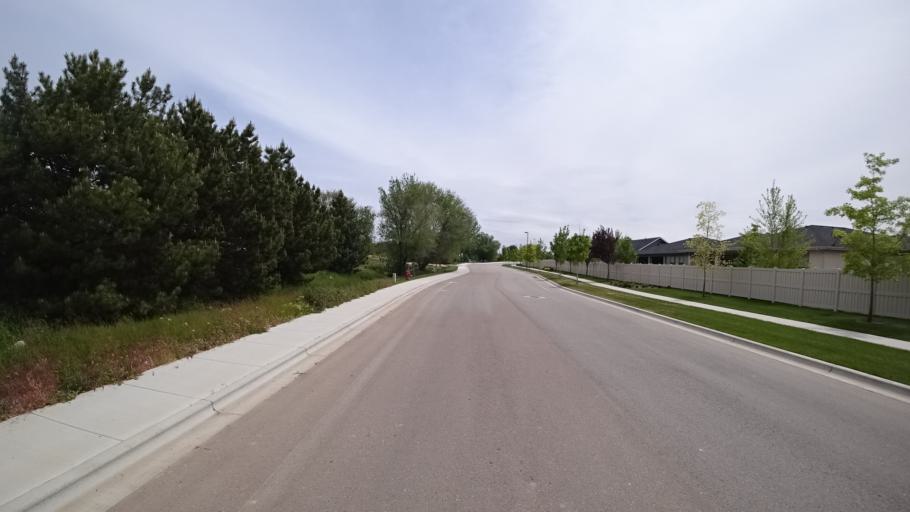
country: US
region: Idaho
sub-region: Ada County
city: Meridian
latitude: 43.5665
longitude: -116.3509
